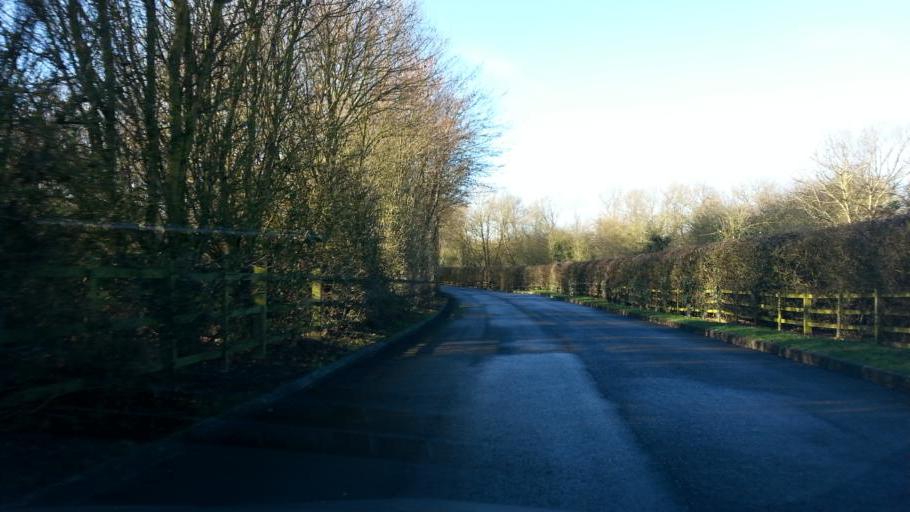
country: GB
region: England
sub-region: Leicestershire
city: Queniborough
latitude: 52.7205
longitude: -1.0557
